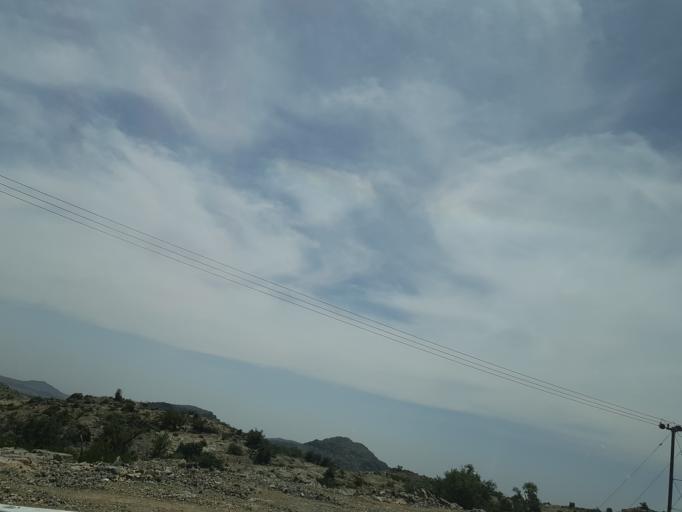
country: OM
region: Muhafazat ad Dakhiliyah
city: Nizwa
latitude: 23.1157
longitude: 57.6427
